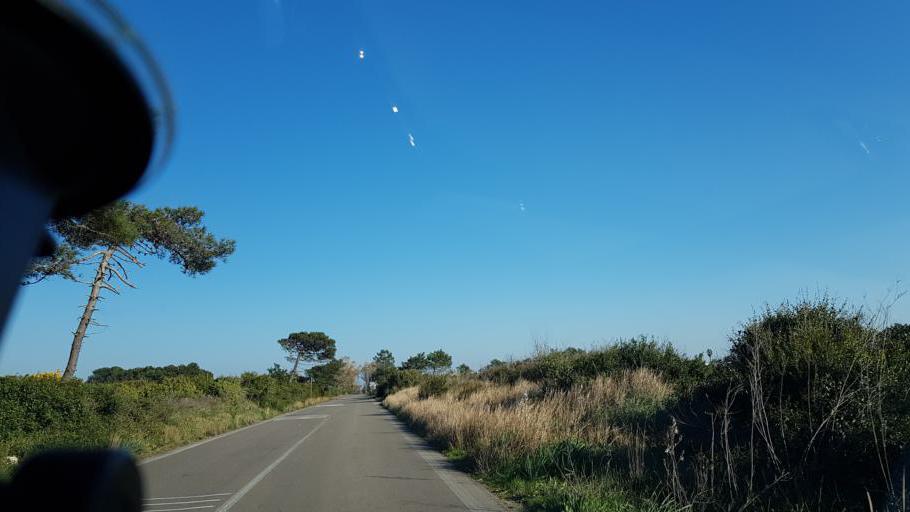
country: IT
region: Apulia
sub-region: Provincia di Lecce
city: Giorgilorio
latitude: 40.4559
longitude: 18.2122
